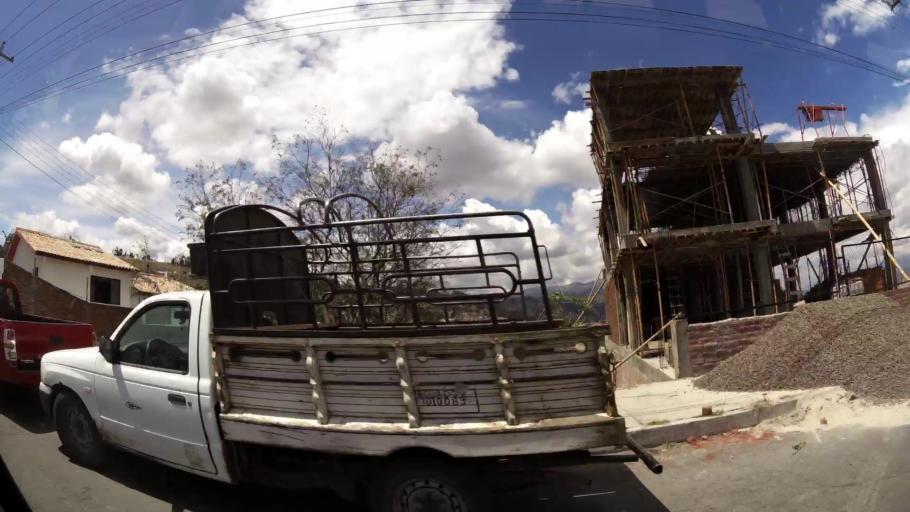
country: EC
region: Tungurahua
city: Ambato
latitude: -1.2797
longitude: -78.6378
